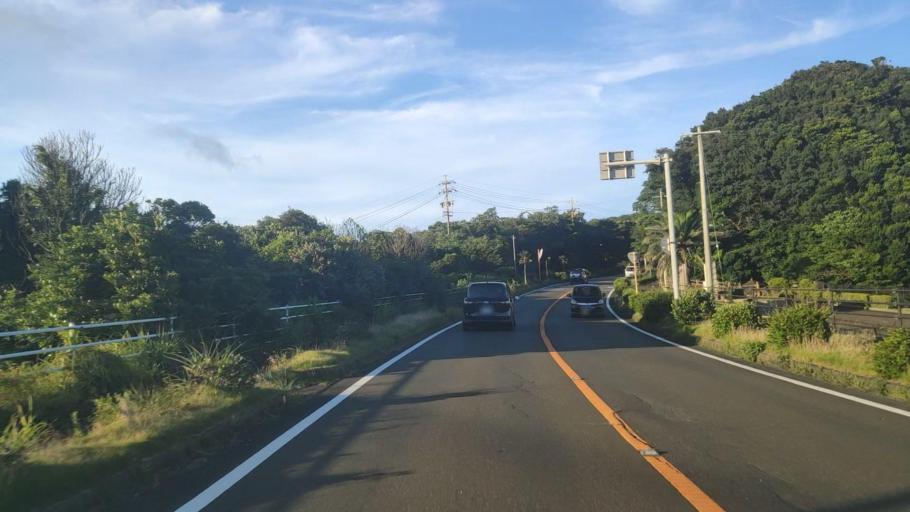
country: JP
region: Mie
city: Toba
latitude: 34.2738
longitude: 136.8698
